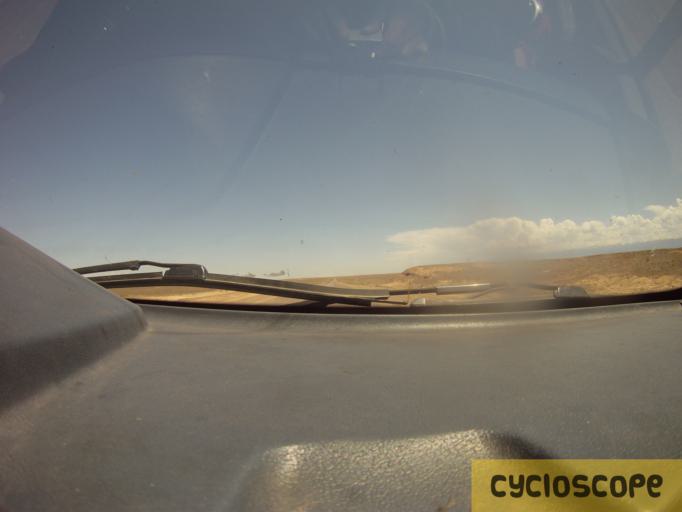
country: KZ
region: Almaty Oblysy
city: Kegen
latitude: 43.5287
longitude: 79.3551
